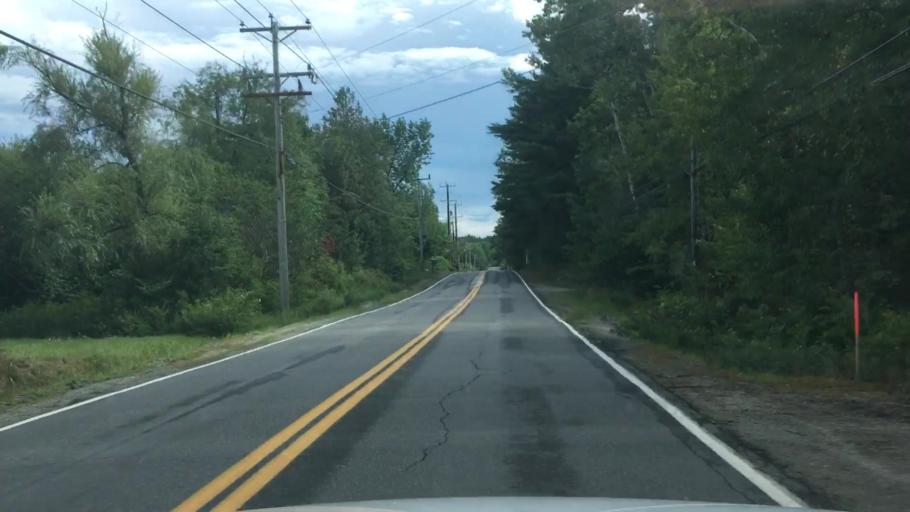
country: US
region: Maine
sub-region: Hancock County
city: Ellsworth
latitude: 44.4882
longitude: -68.4201
